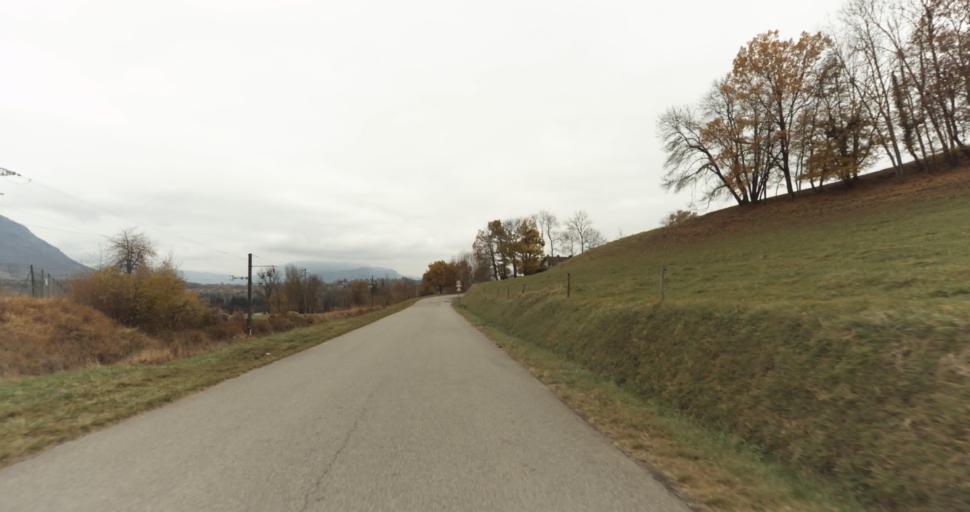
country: FR
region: Rhone-Alpes
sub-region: Departement de la Haute-Savoie
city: Saint-Martin-Bellevue
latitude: 45.9491
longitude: 6.1562
